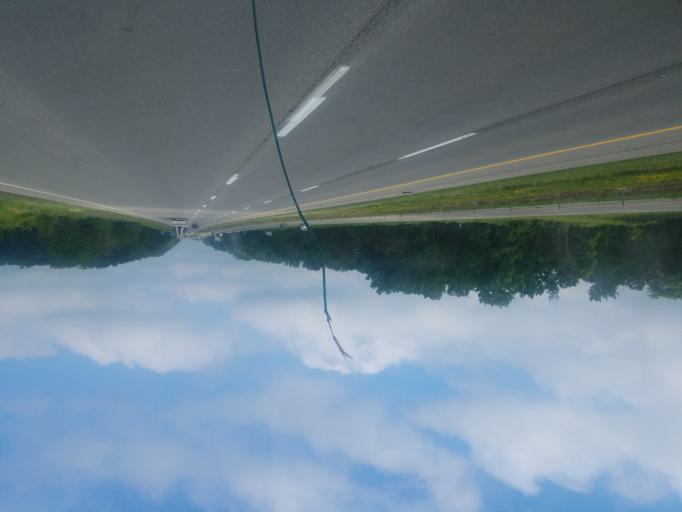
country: US
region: Ohio
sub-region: Morrow County
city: Mount Gilead
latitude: 40.4937
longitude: -82.7238
